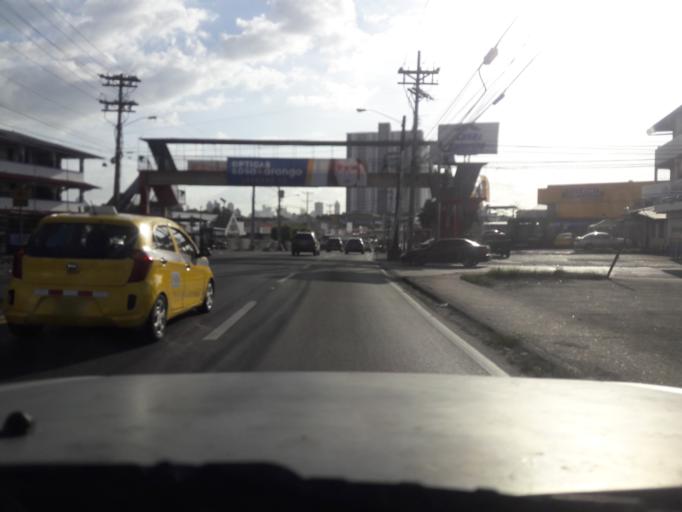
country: PA
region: Panama
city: Panama
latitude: 9.0191
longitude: -79.4924
